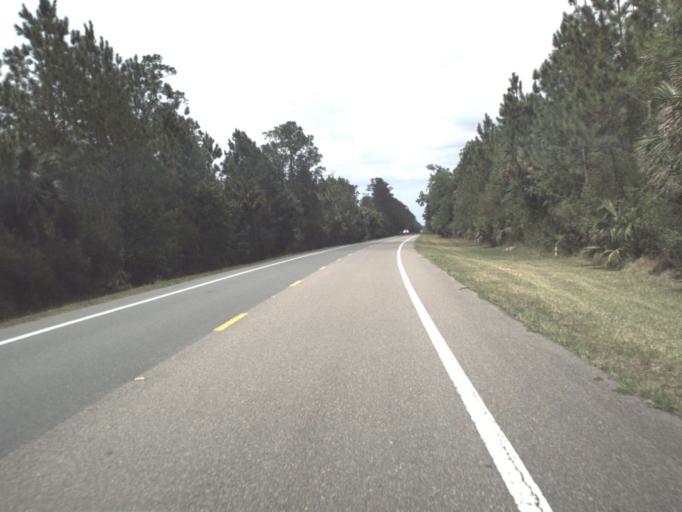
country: US
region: Florida
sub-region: Flagler County
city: Bunnell
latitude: 29.3718
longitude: -81.3117
